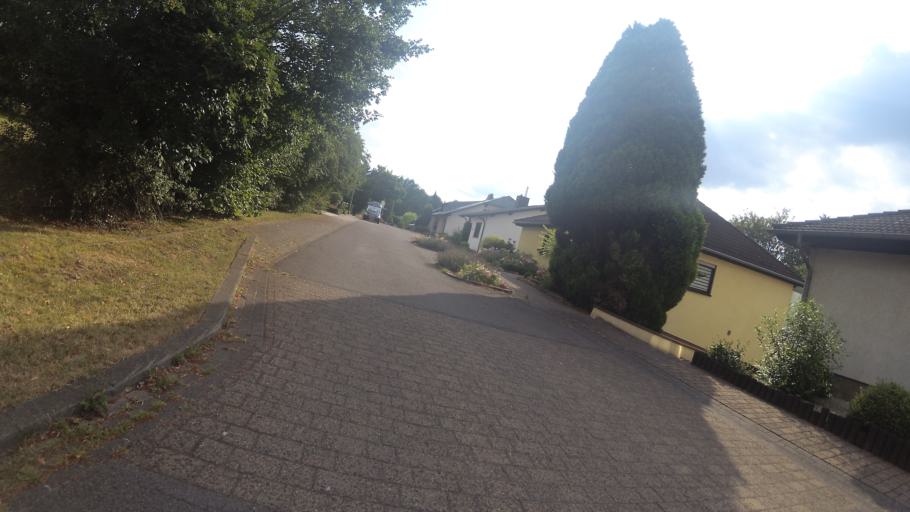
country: DE
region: Saarland
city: Illingen
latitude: 49.3745
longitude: 7.0136
